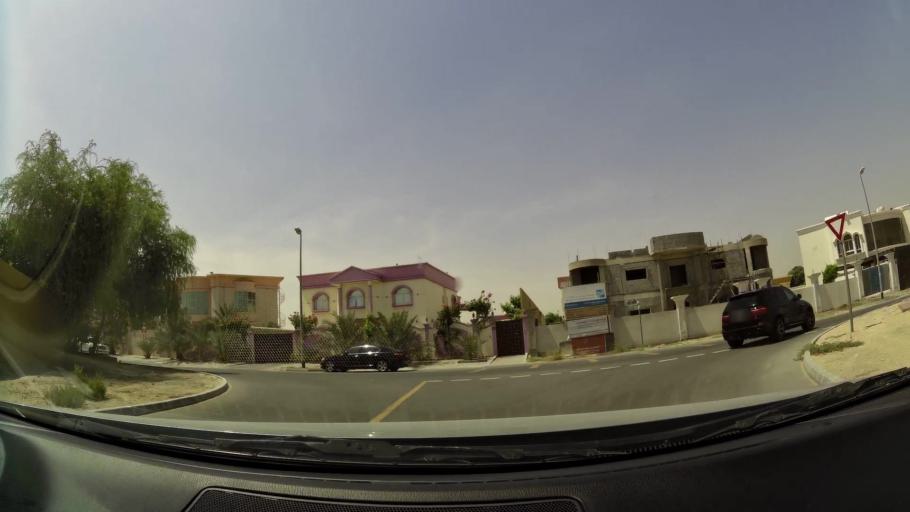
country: AE
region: Ash Shariqah
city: Sharjah
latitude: 25.1818
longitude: 55.4189
